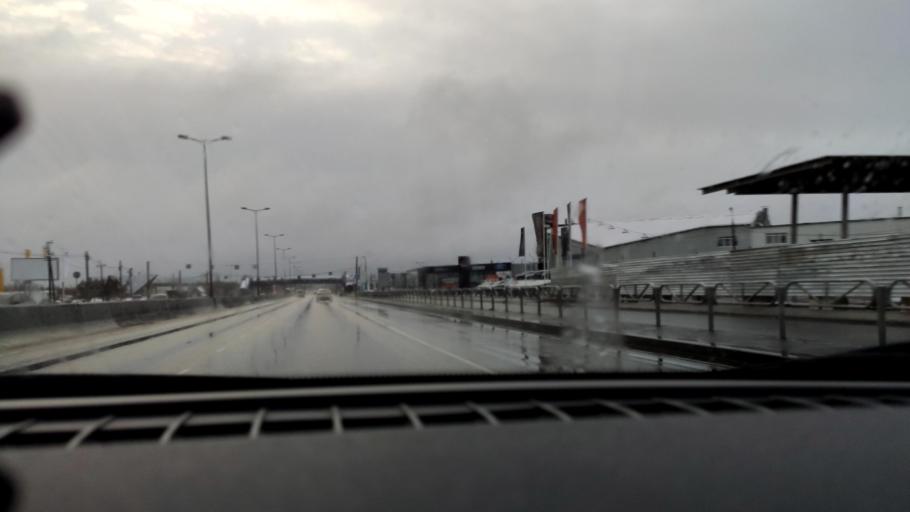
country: RU
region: Perm
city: Perm
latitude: 58.0365
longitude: 56.1955
